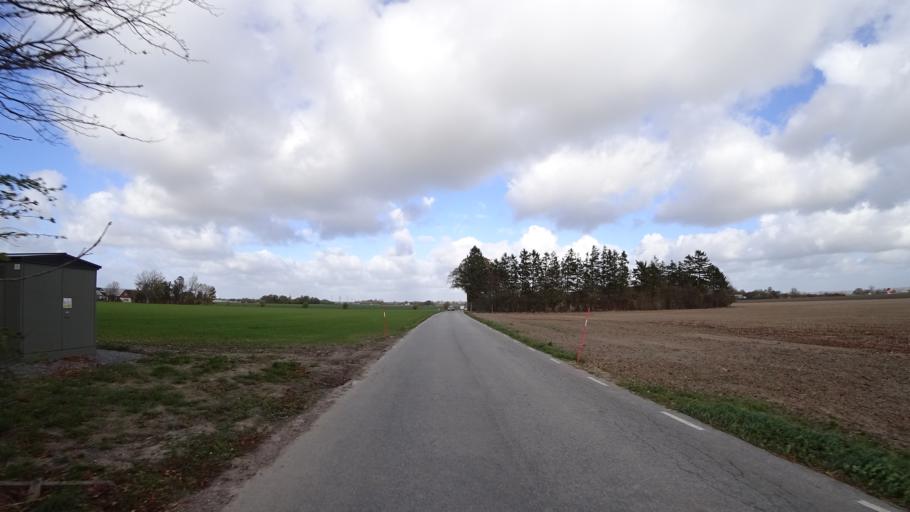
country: SE
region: Skane
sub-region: Staffanstorps Kommun
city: Hjaerup
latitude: 55.6524
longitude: 13.1570
